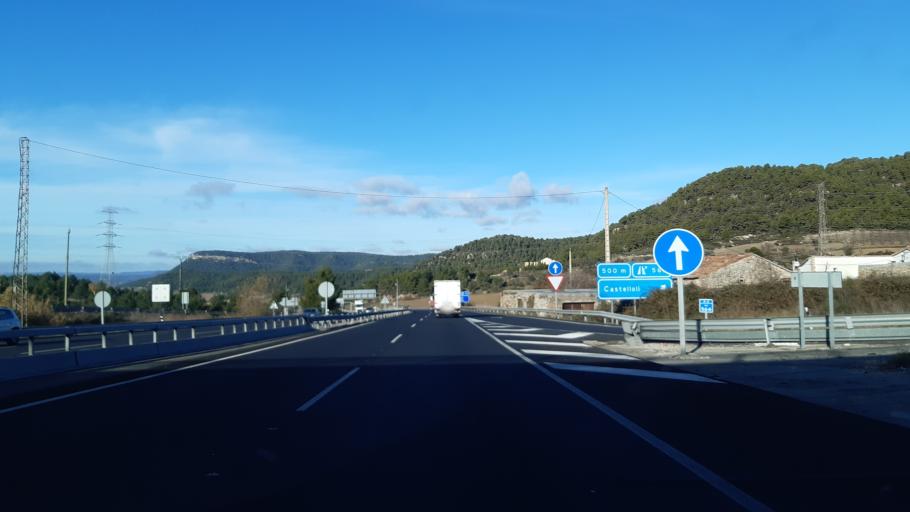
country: ES
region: Catalonia
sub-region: Provincia de Barcelona
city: Castelloli
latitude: 41.5955
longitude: 1.7203
